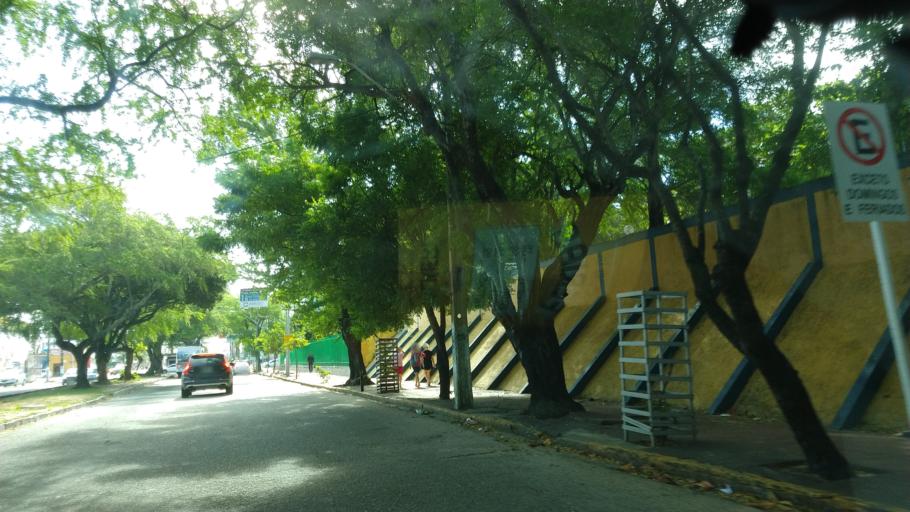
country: BR
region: Rio Grande do Norte
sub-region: Natal
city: Natal
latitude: -5.8131
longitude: -35.2040
